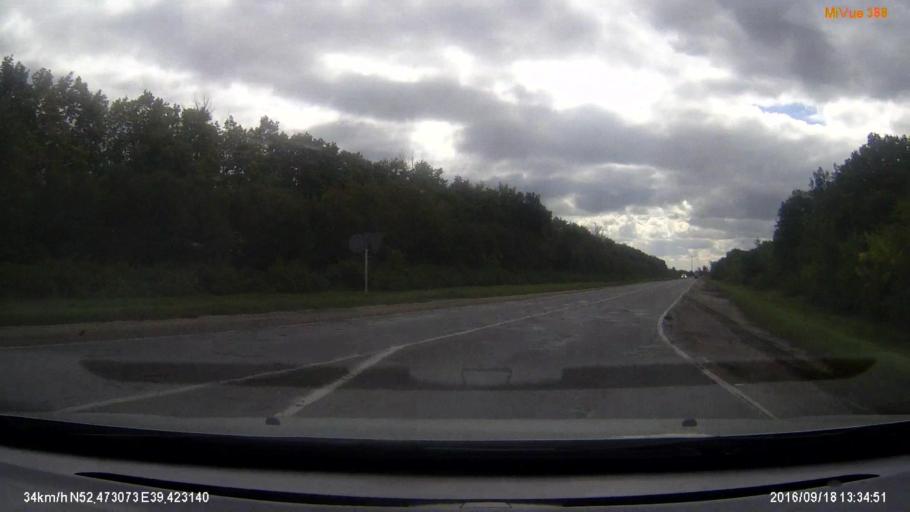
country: RU
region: Lipetsk
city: Borinskoye
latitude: 52.4505
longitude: 39.3737
